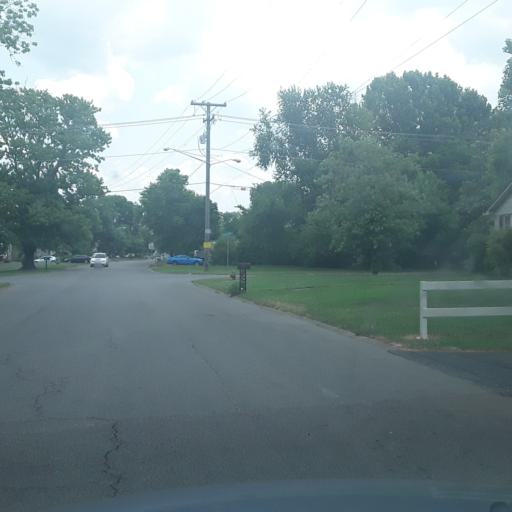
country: US
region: Tennessee
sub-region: Williamson County
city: Brentwood Estates
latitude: 36.0529
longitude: -86.6976
